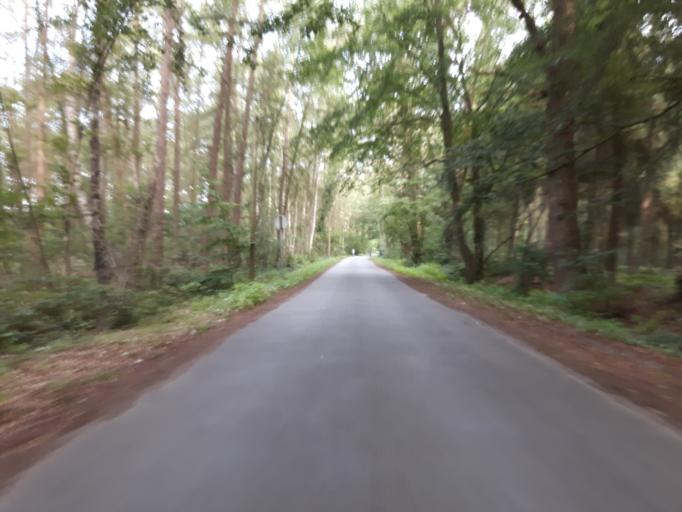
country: DE
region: Lower Saxony
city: Delmenhorst
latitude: 53.0822
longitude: 8.6350
